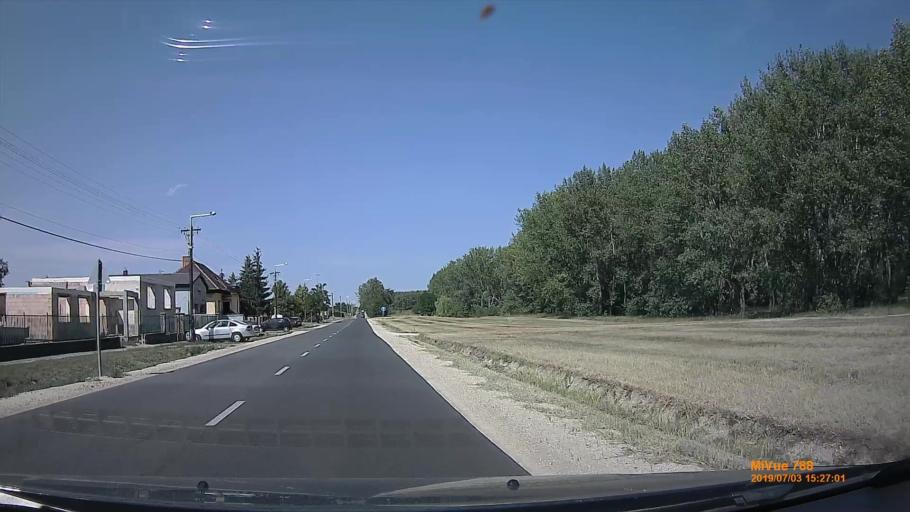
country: HU
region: Gyor-Moson-Sopron
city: Gyor
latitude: 47.7169
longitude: 17.6548
